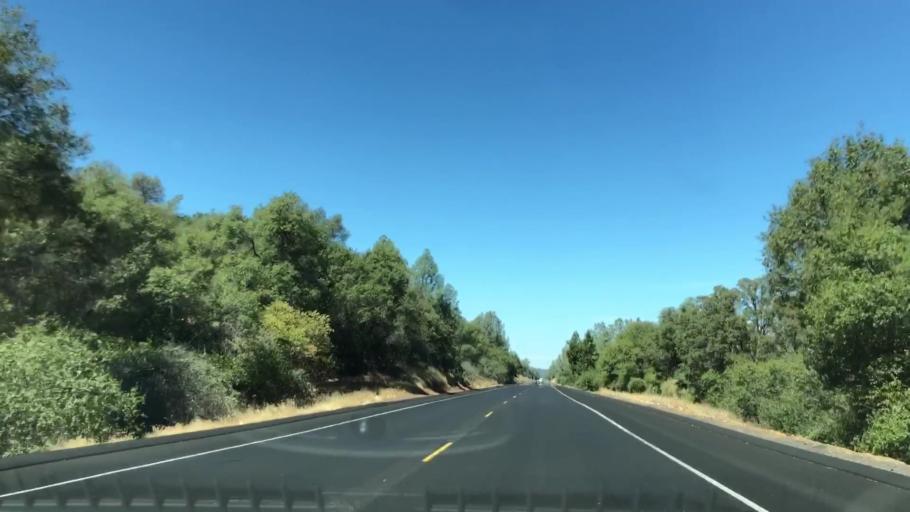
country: US
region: California
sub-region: Tuolumne County
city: East Sonora
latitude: 37.8216
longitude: -120.3288
